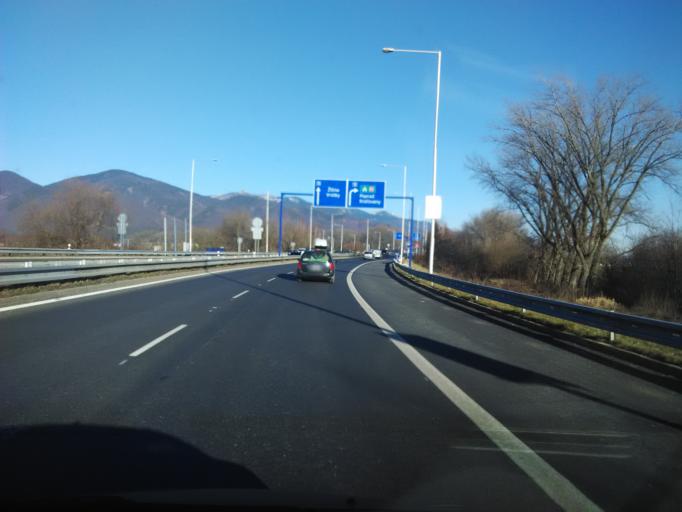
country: SK
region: Zilinsky
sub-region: Okres Zilina
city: Vrutky
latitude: 49.0915
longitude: 18.9218
